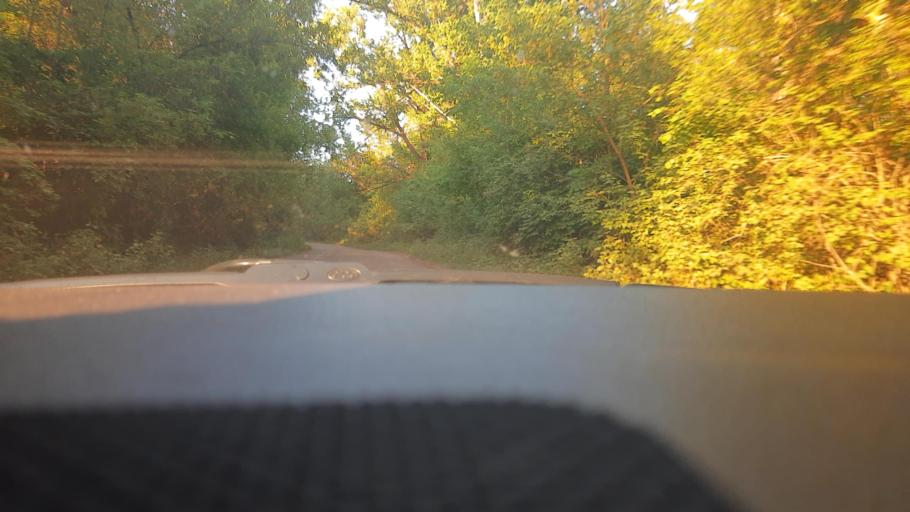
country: RU
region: Bashkortostan
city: Chishmy
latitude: 54.6328
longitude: 55.5420
